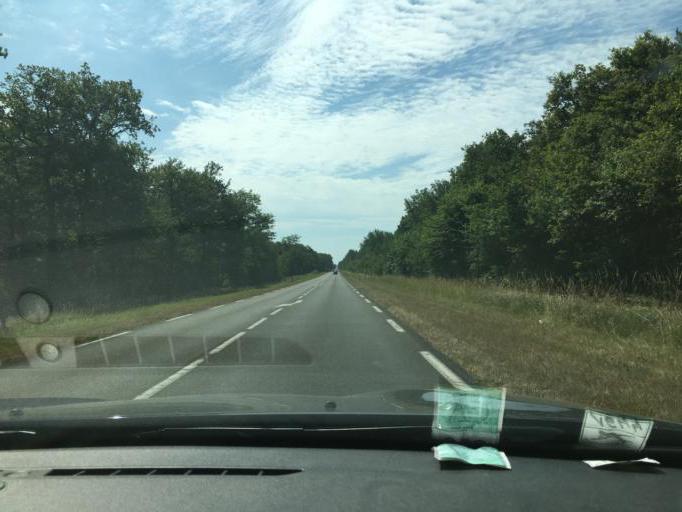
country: FR
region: Centre
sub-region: Departement du Loiret
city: La Ferte-Saint-Aubin
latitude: 47.6837
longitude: 1.9622
